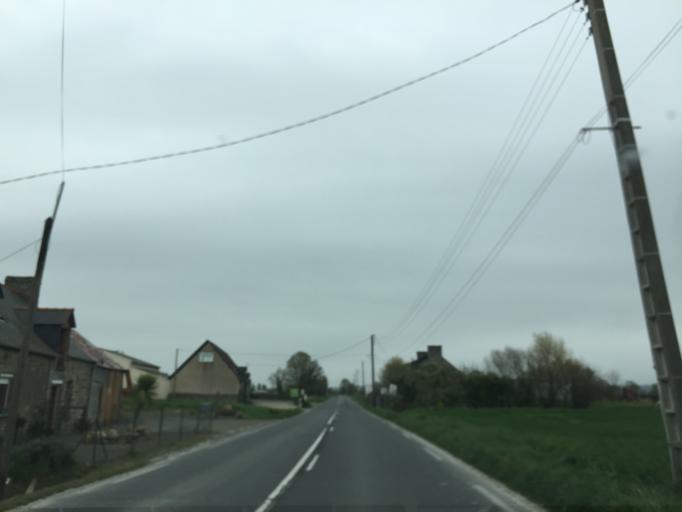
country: FR
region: Brittany
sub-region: Departement d'Ille-et-Vilaine
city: Cherrueix
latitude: 48.6005
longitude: -1.7032
